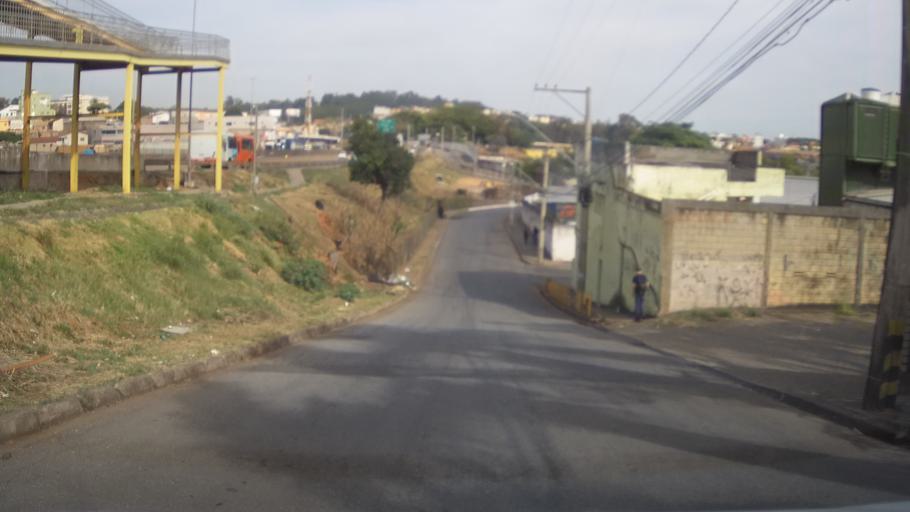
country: BR
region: Minas Gerais
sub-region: Contagem
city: Contagem
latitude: -19.9599
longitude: -44.0528
